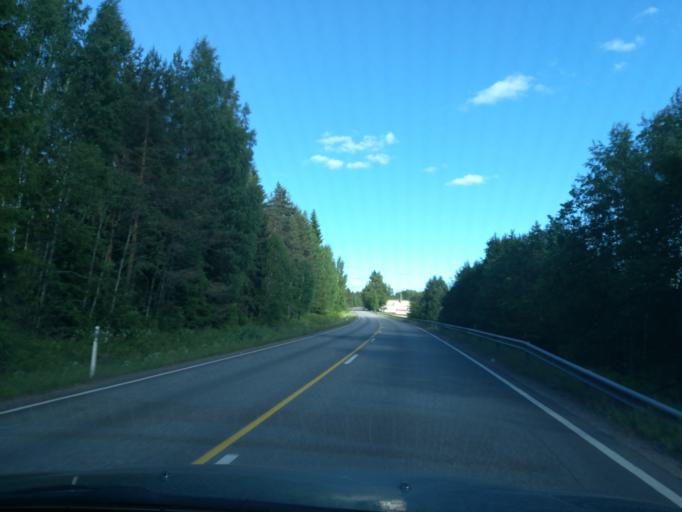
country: FI
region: South Karelia
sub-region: Imatra
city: Ruokolahti
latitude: 61.3737
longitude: 28.6621
